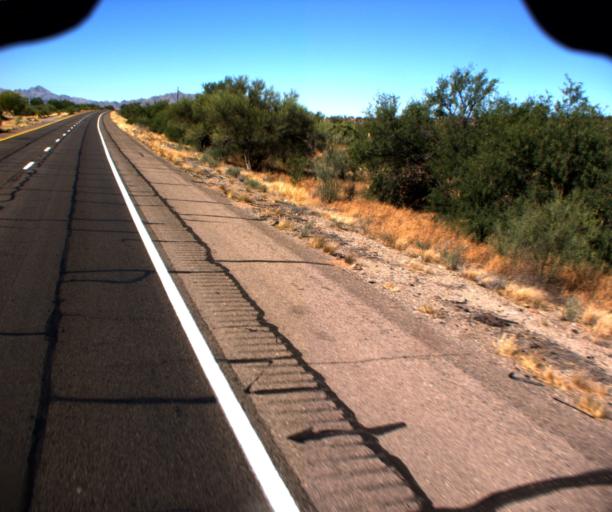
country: US
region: Arizona
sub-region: Pima County
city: Arivaca Junction
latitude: 31.7443
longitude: -111.0473
